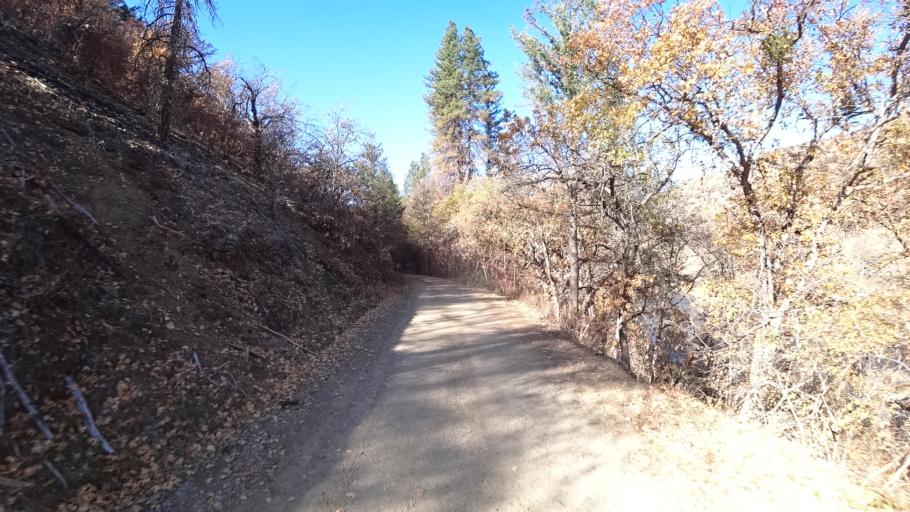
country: US
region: California
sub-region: Siskiyou County
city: Yreka
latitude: 41.8625
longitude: -122.7246
